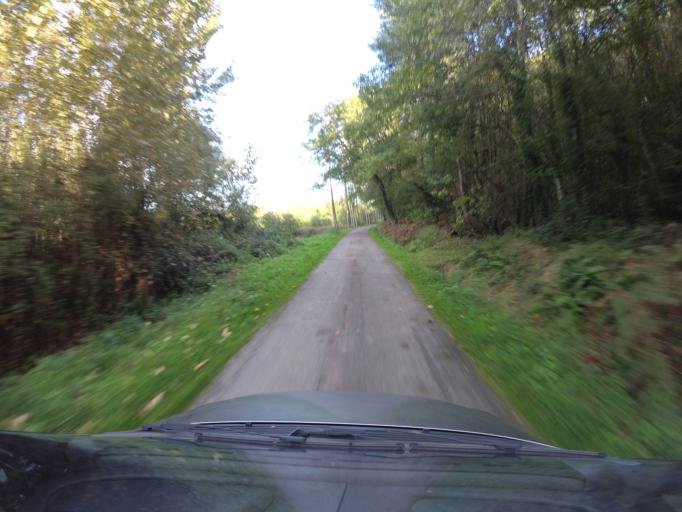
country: FR
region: Brittany
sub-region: Departement du Morbihan
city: Peillac
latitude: 47.7278
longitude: -2.2272
